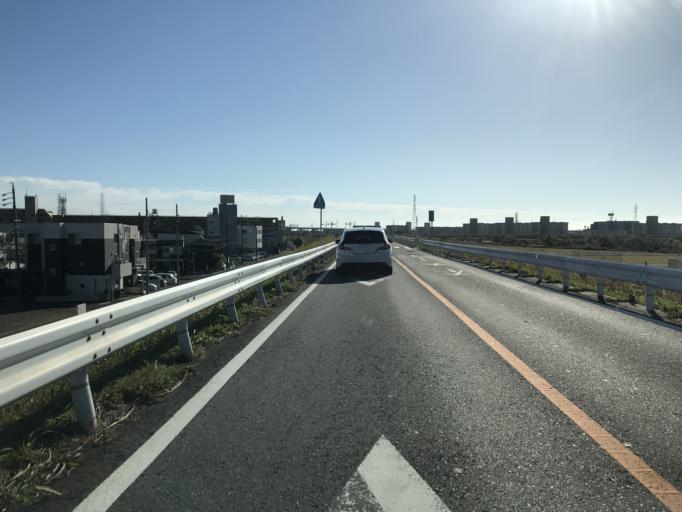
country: JP
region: Aichi
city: Kanie
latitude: 35.1675
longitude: 136.8363
